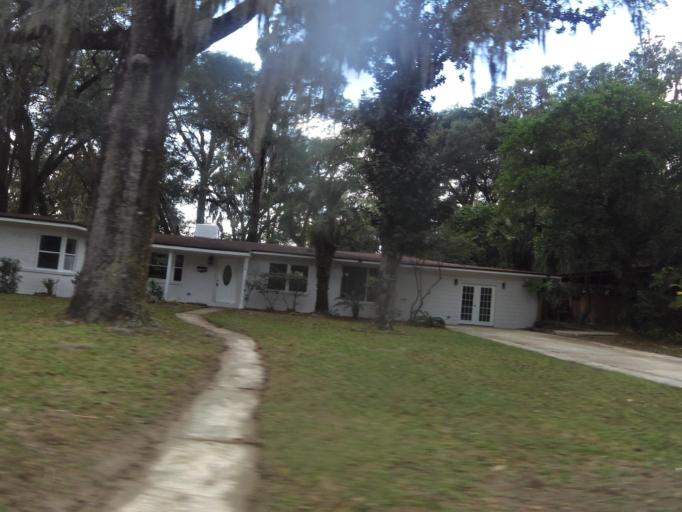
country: US
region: Florida
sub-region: Duval County
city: Jacksonville
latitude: 30.3237
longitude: -81.5914
